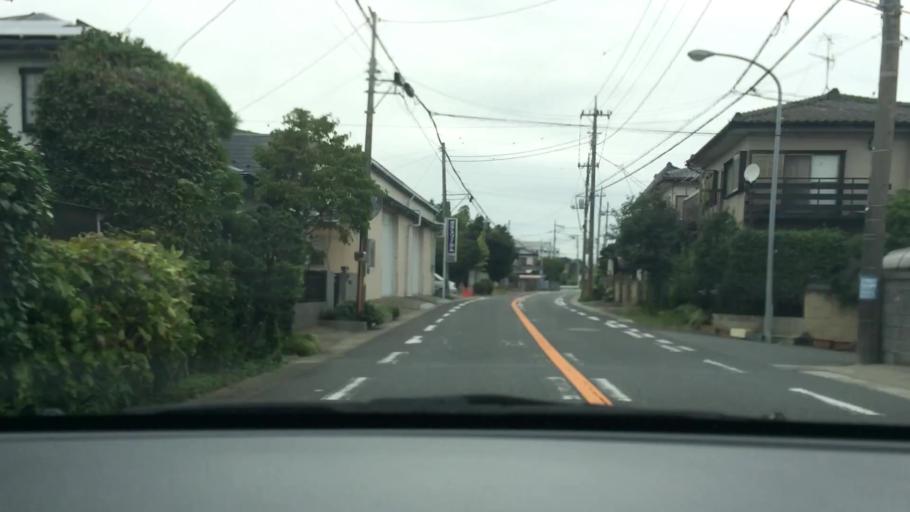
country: JP
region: Chiba
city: Nagareyama
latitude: 35.8636
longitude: 139.9021
